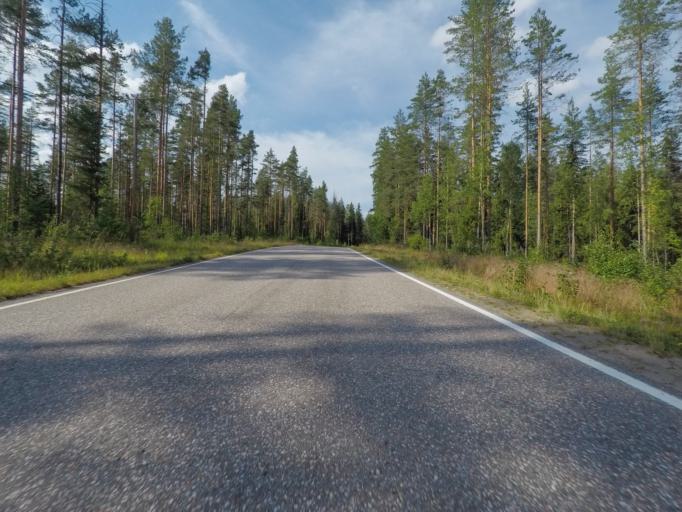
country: FI
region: Southern Savonia
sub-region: Savonlinna
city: Sulkava
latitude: 61.7666
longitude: 28.2359
